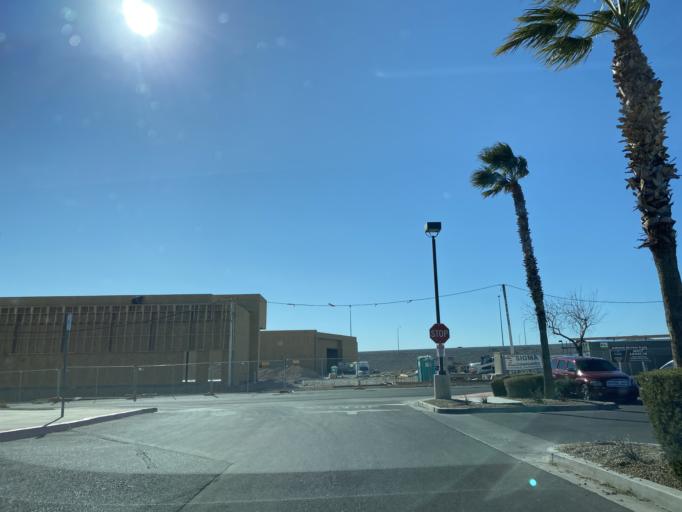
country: US
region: Nevada
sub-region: Clark County
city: Summerlin South
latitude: 36.2812
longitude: -115.2844
